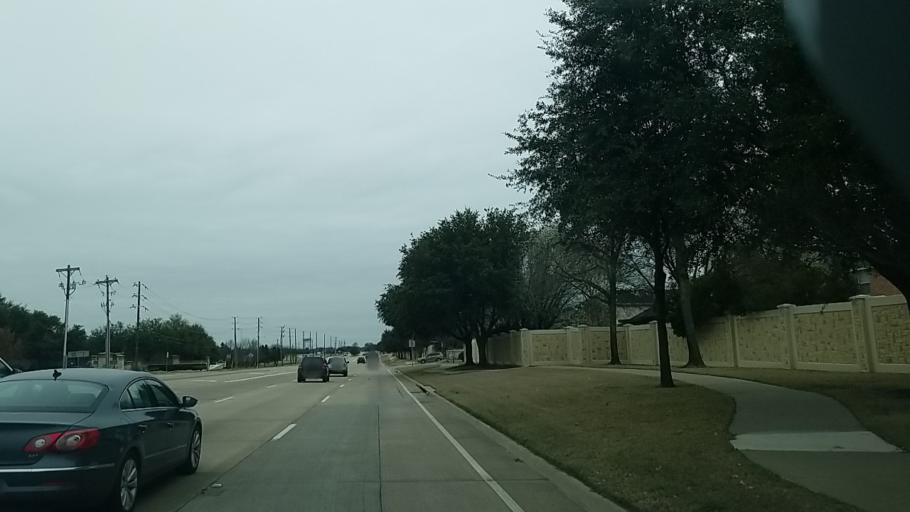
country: US
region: Texas
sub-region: Denton County
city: Flower Mound
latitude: 33.0115
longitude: -97.0709
